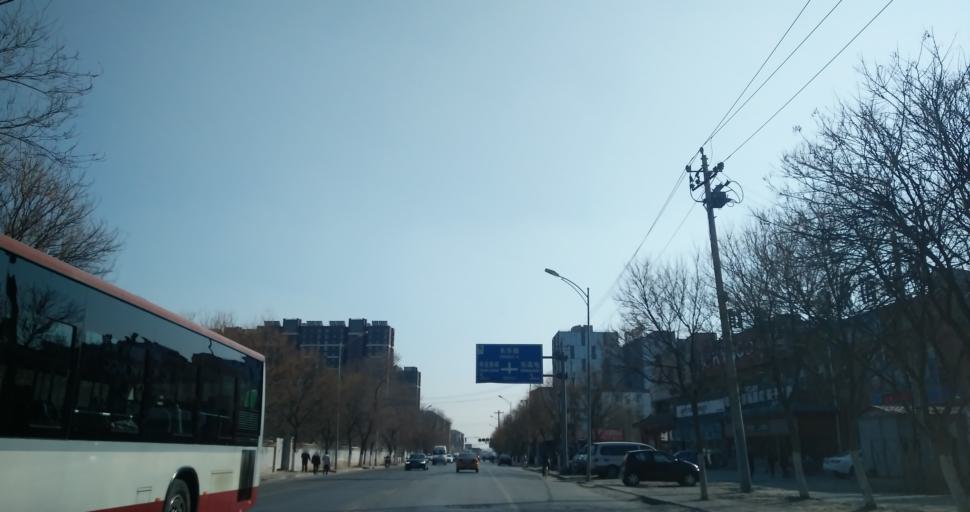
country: CN
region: Beijing
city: Jiugong
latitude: 39.8081
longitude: 116.4497
